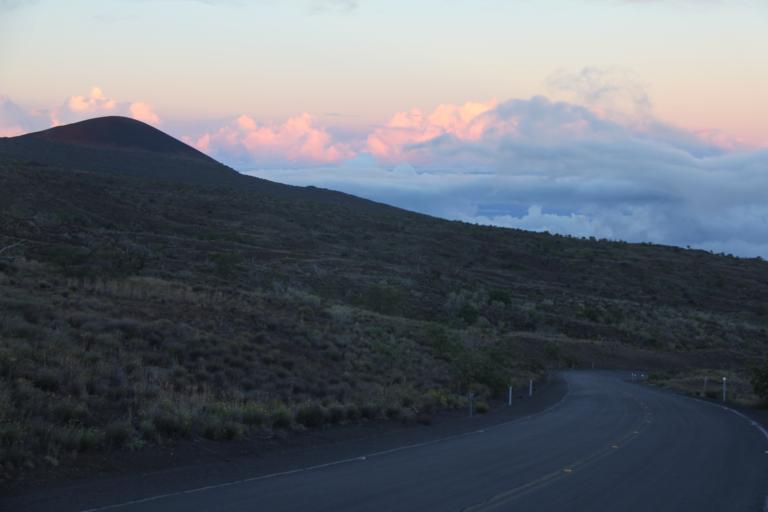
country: US
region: Hawaii
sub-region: Hawaii County
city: Honoka'a
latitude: 19.7448
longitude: -155.4521
